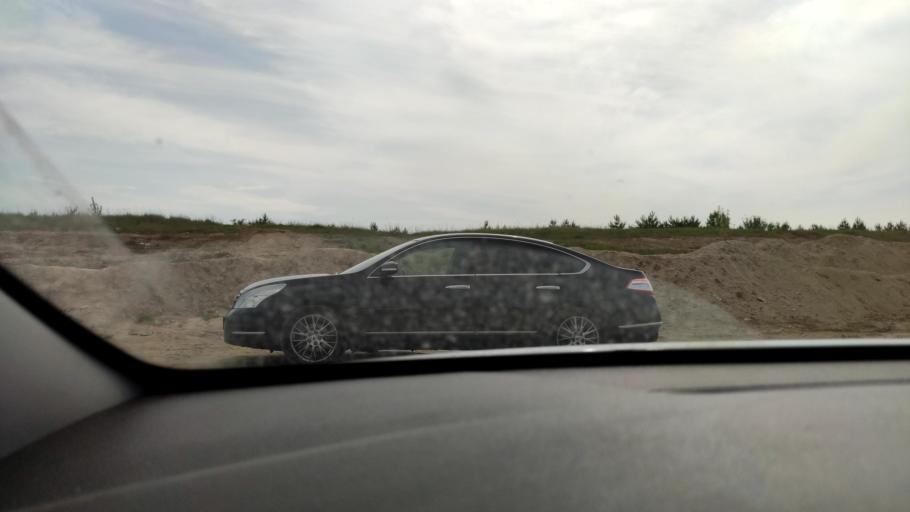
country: RU
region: Tatarstan
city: Vysokaya Gora
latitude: 55.7901
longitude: 49.2662
